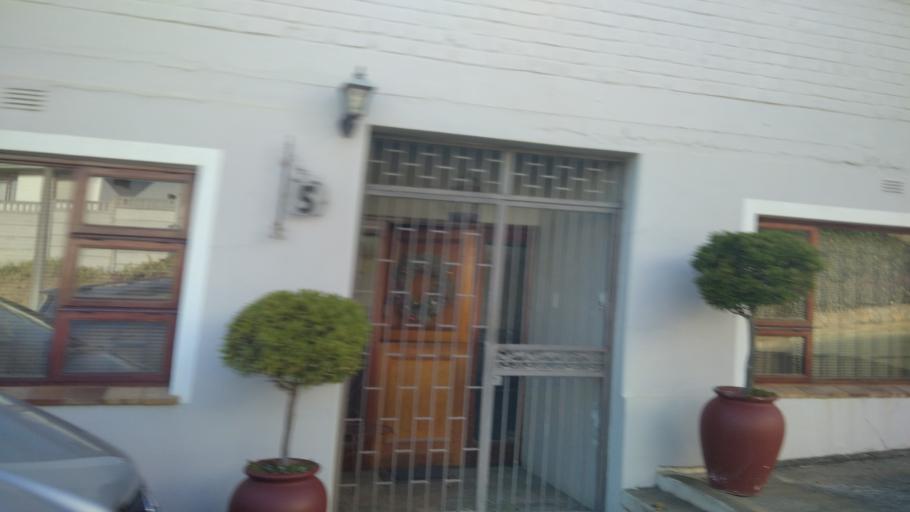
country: ZA
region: Western Cape
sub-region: Overberg District Municipality
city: Caledon
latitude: -34.2305
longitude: 19.4304
